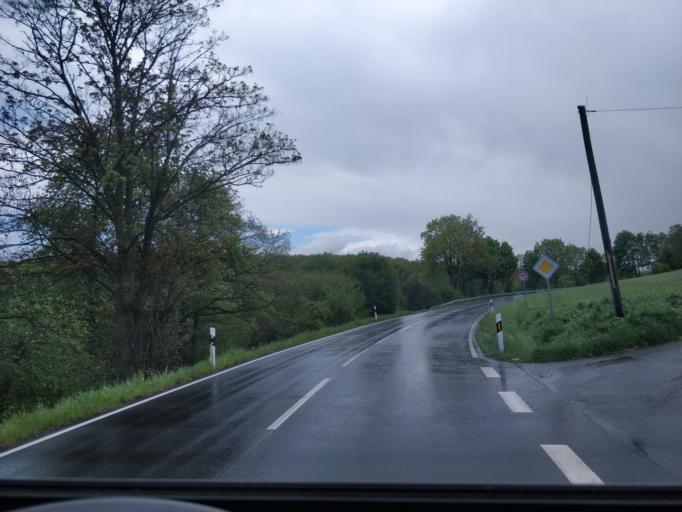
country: DE
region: North Rhine-Westphalia
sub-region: Regierungsbezirk Koln
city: Rheinbach
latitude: 50.5963
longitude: 6.8965
